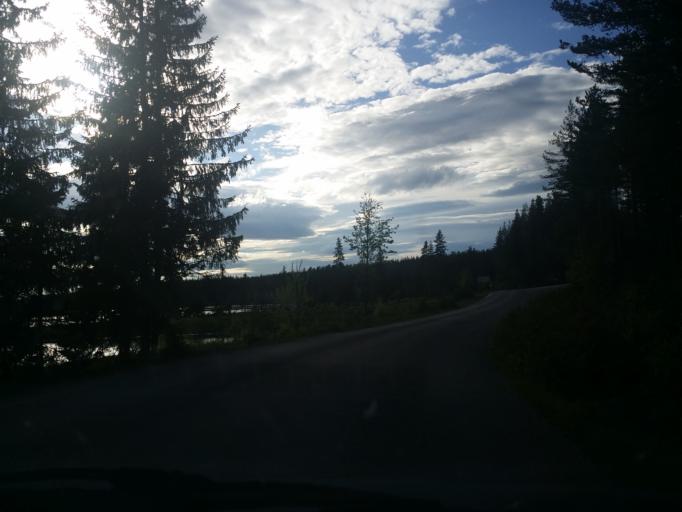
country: NO
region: Hedmark
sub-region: Ringsaker
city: Brumunddal
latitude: 61.0356
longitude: 10.9411
